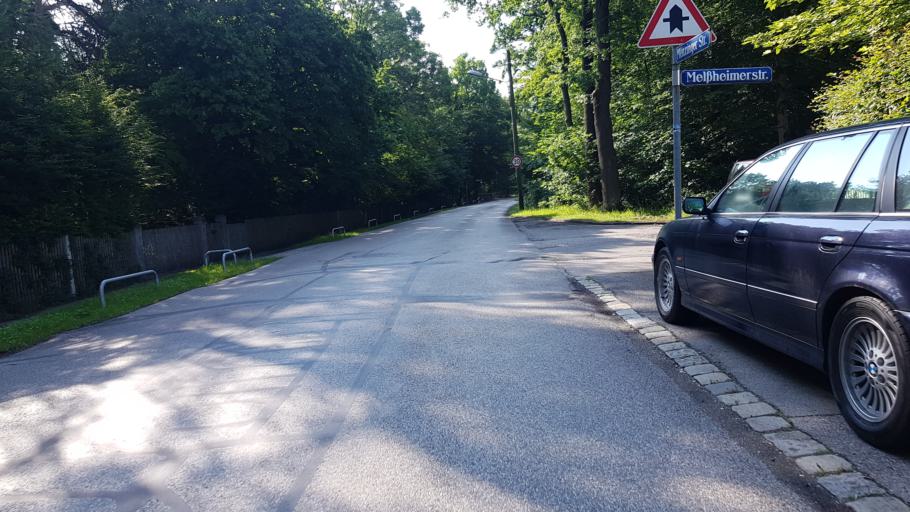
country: DE
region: Bavaria
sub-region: Upper Bavaria
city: Pasing
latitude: 48.1698
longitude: 11.4835
